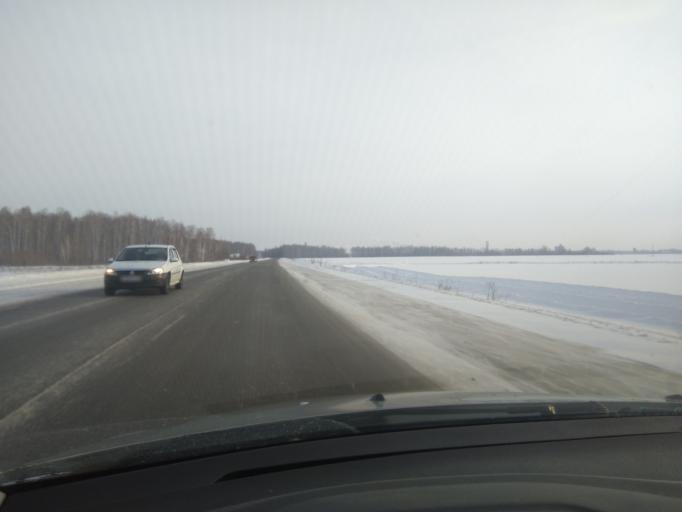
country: RU
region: Sverdlovsk
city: Bogdanovich
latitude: 56.7981
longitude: 62.0091
